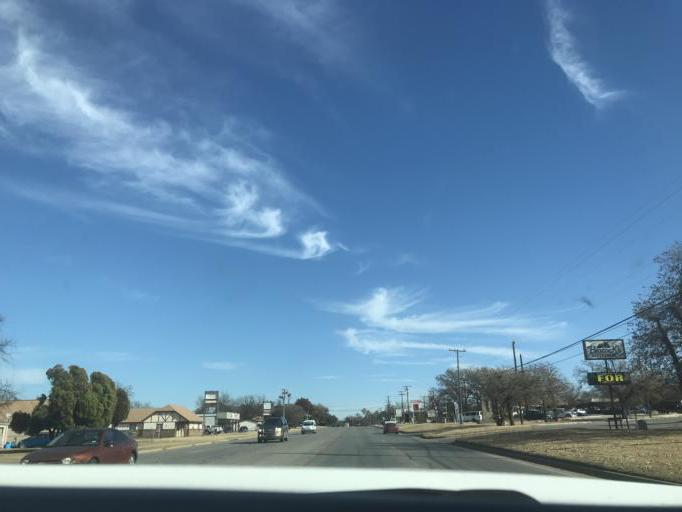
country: US
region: Texas
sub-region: Erath County
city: Stephenville
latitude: 32.2256
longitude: -98.2300
